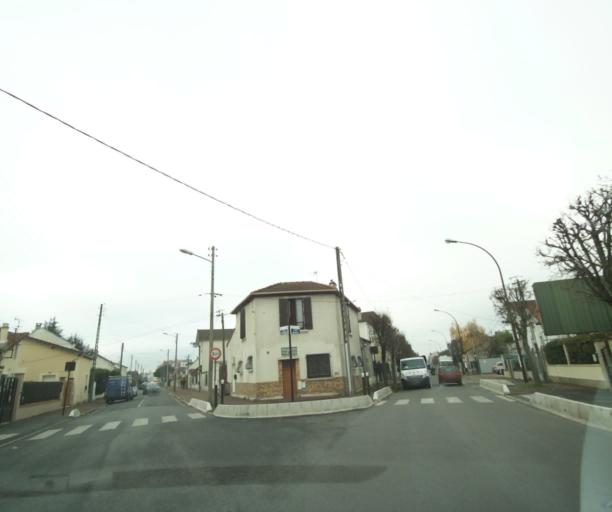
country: FR
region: Ile-de-France
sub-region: Departement de Seine-Saint-Denis
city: Livry-Gargan
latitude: 48.9259
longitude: 2.5277
